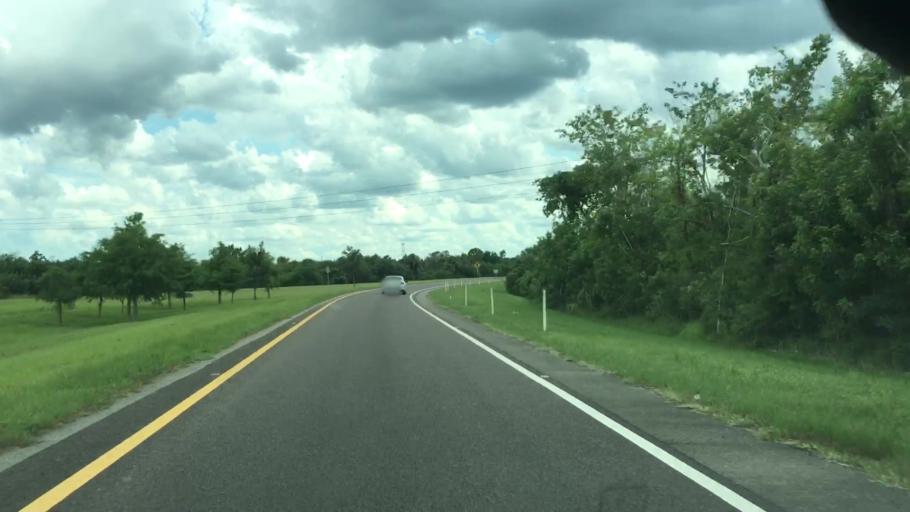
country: US
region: Florida
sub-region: Brevard County
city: Port Saint John
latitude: 28.4987
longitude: -80.8418
